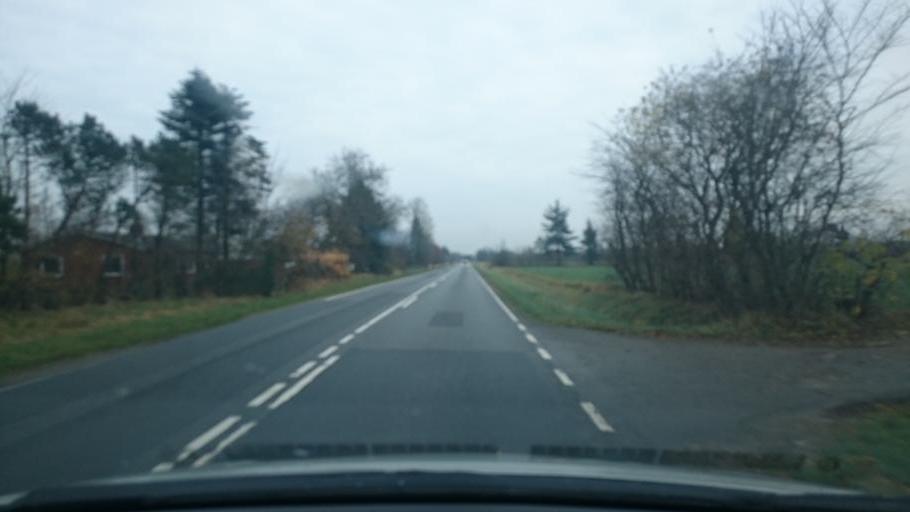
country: DK
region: South Denmark
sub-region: Esbjerg Kommune
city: Ribe
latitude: 55.3328
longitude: 8.8863
